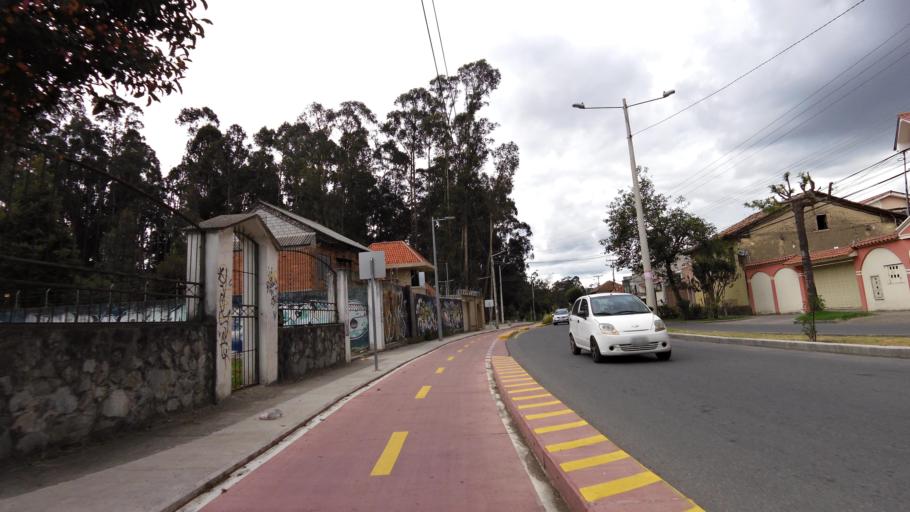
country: EC
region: Azuay
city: Cuenca
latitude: -2.9069
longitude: -79.0257
